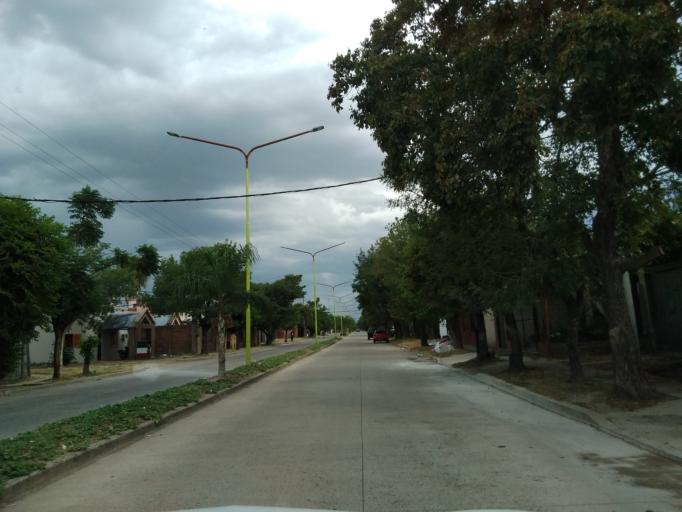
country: AR
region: Corrientes
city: Corrientes
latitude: -27.5182
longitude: -58.7916
